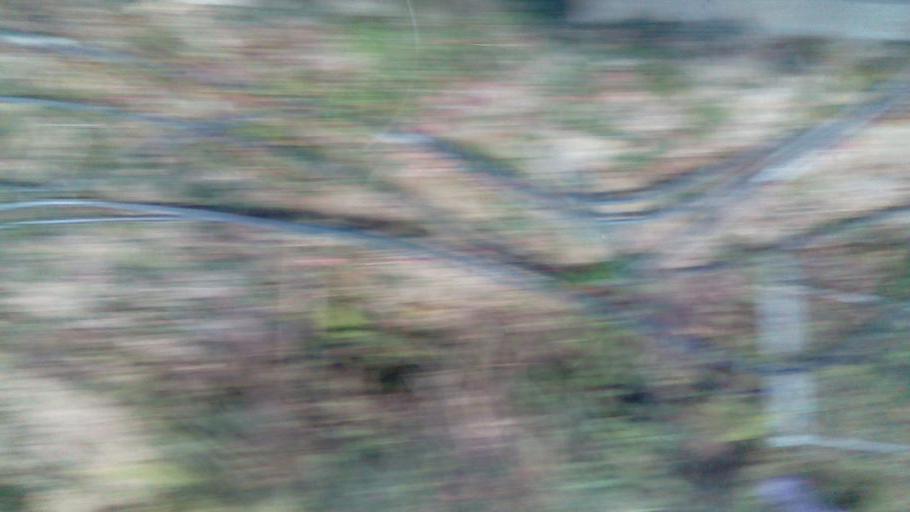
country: TW
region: Taiwan
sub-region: Hualien
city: Hualian
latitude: 24.3439
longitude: 121.3184
